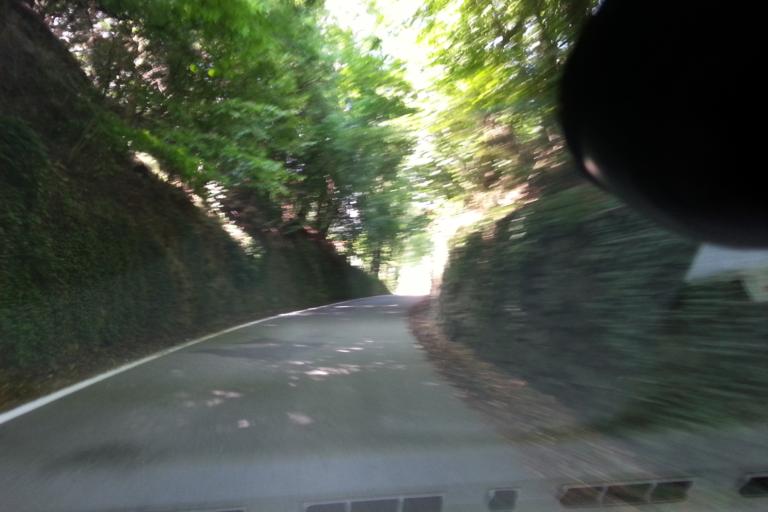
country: IT
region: Piedmont
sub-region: Provincia di Torino
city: Valgioie
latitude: 45.0755
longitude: 7.3595
